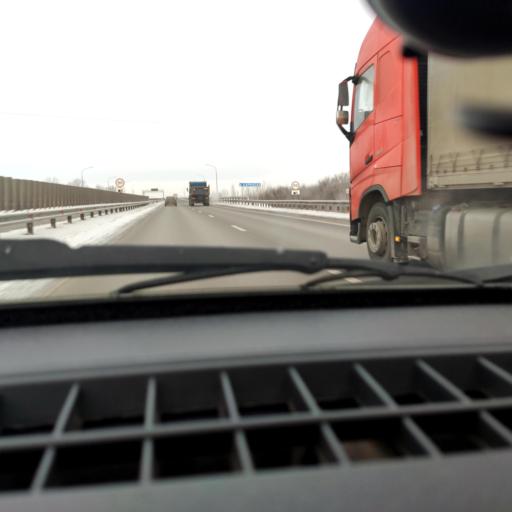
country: RU
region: Bashkortostan
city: Asanovo
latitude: 54.9703
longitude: 55.5781
